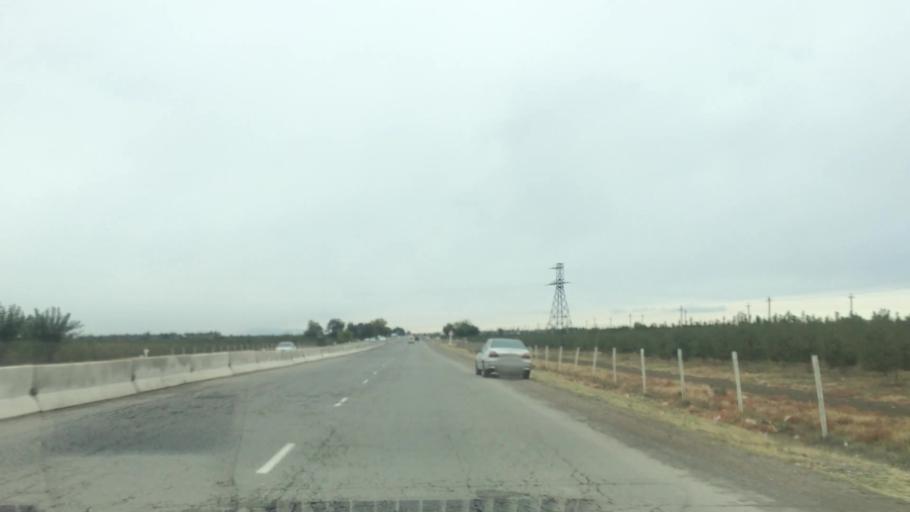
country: UZ
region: Samarqand
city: Bulung'ur
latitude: 39.7557
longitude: 67.2403
